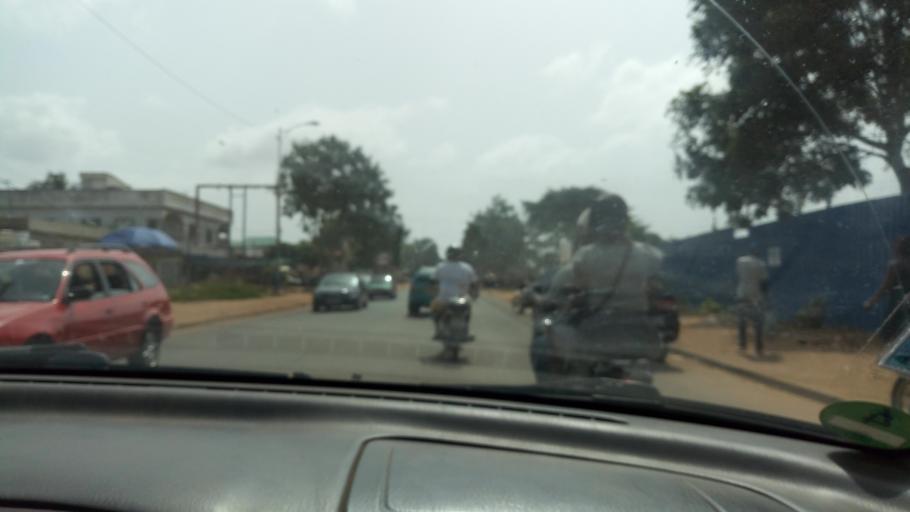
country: TG
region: Maritime
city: Lome
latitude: 6.1783
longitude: 1.1759
